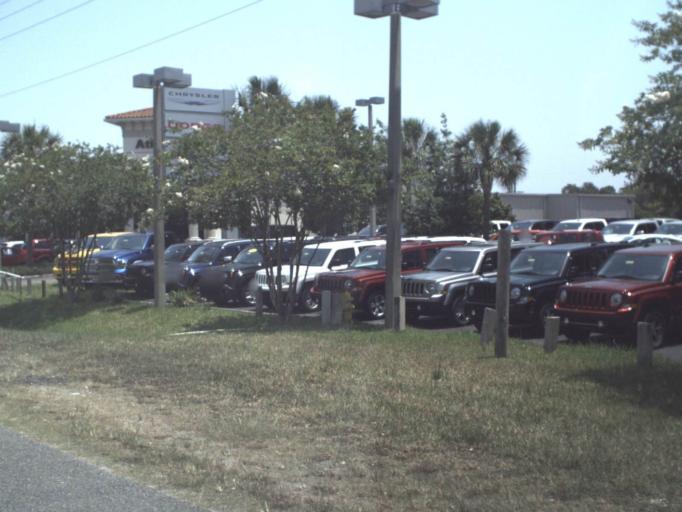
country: US
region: Florida
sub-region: Saint Johns County
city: Saint Augustine South
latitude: 29.8557
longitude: -81.3227
